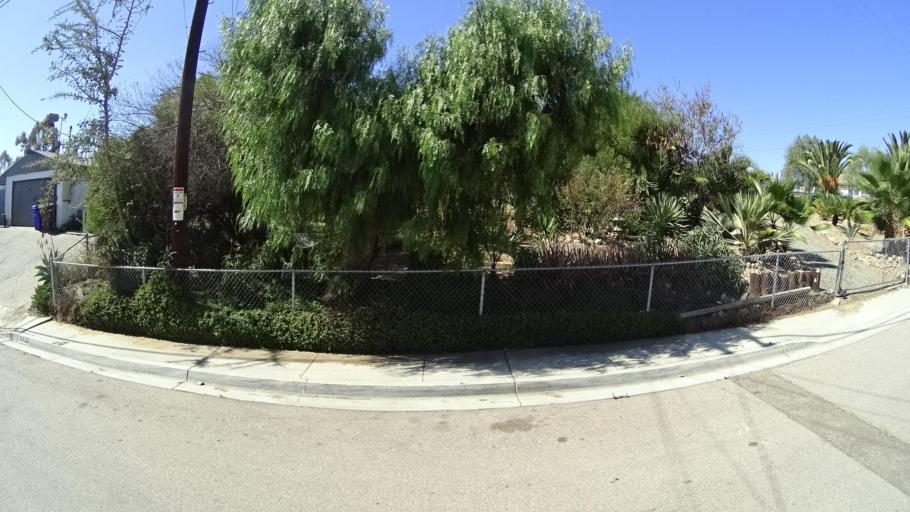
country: US
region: California
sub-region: San Diego County
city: National City
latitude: 32.6676
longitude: -117.0788
